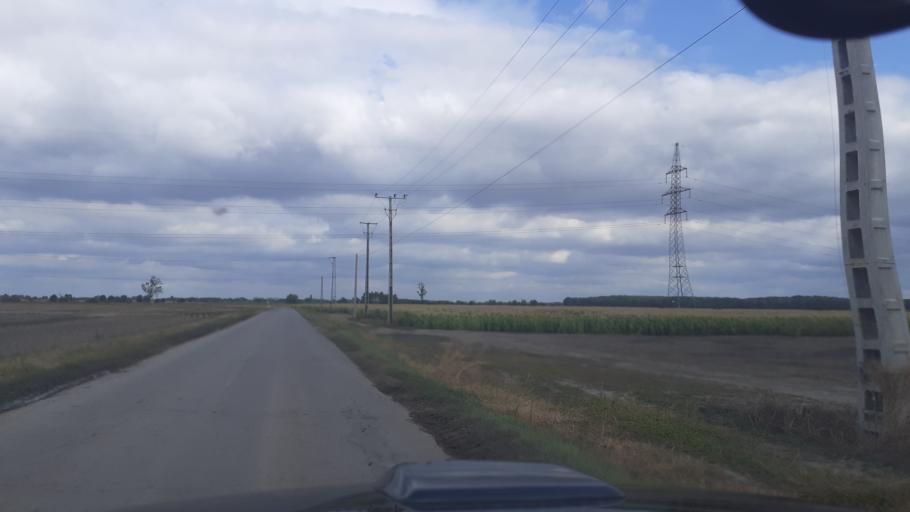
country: HU
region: Bacs-Kiskun
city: Apostag
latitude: 46.8565
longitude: 18.9530
